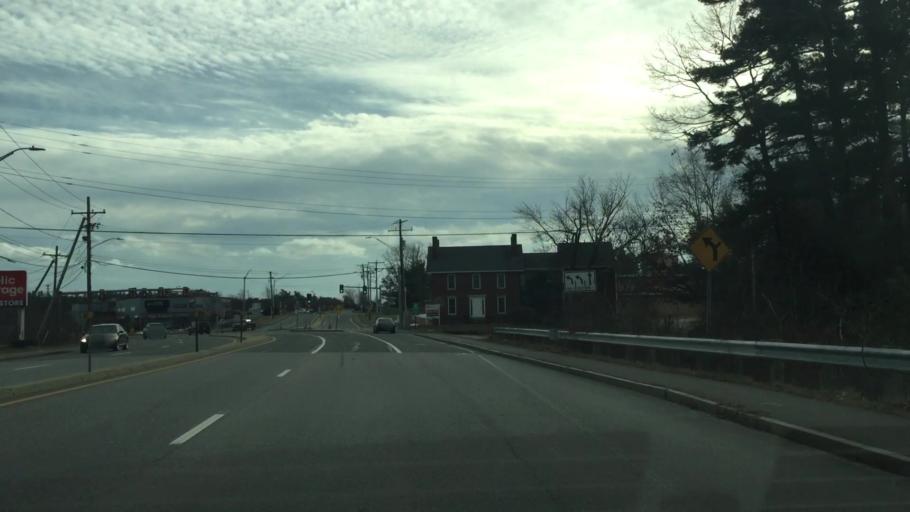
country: US
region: New Hampshire
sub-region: Hillsborough County
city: Manchester
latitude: 42.9471
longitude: -71.4333
